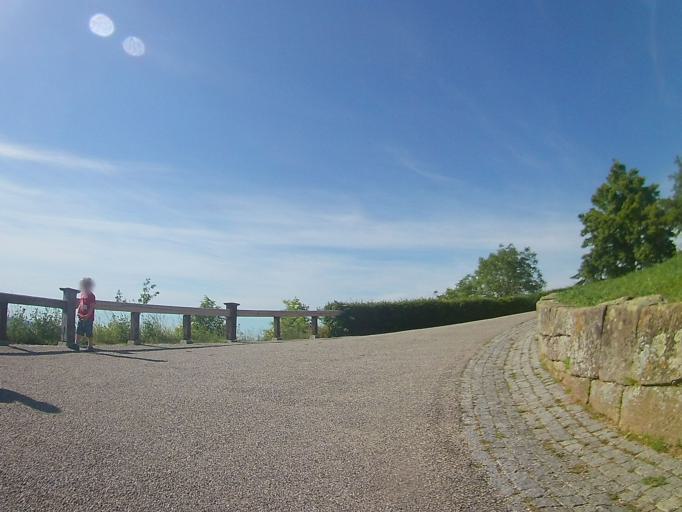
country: DE
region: Baden-Wuerttemberg
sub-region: Regierungsbezirk Stuttgart
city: Fellbach
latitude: 48.7817
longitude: 9.2681
